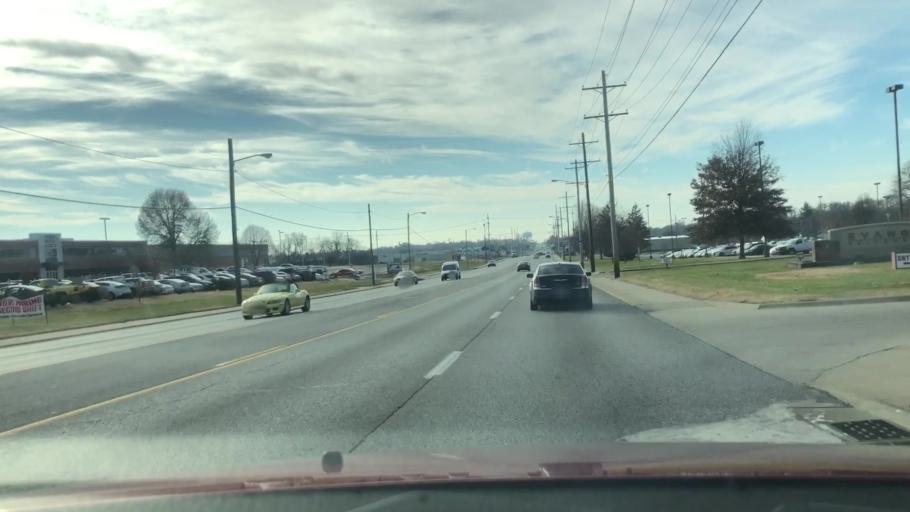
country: US
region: Missouri
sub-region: Greene County
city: Springfield
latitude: 37.2213
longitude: -93.2616
